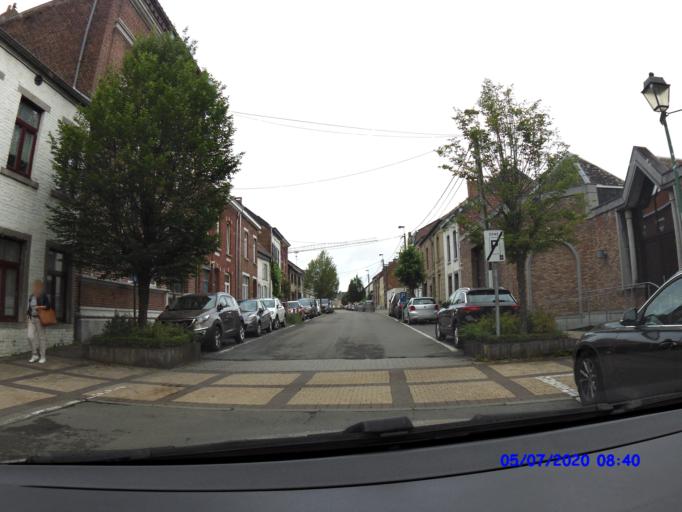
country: BE
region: Wallonia
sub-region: Province du Brabant Wallon
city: Genappe
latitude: 50.6143
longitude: 4.4497
